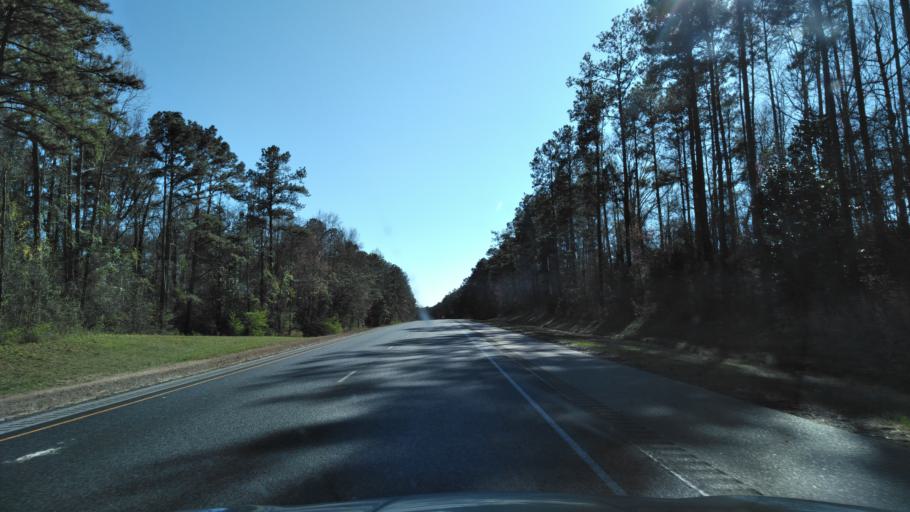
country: US
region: Alabama
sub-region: Butler County
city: Georgiana
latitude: 31.7120
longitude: -86.7335
